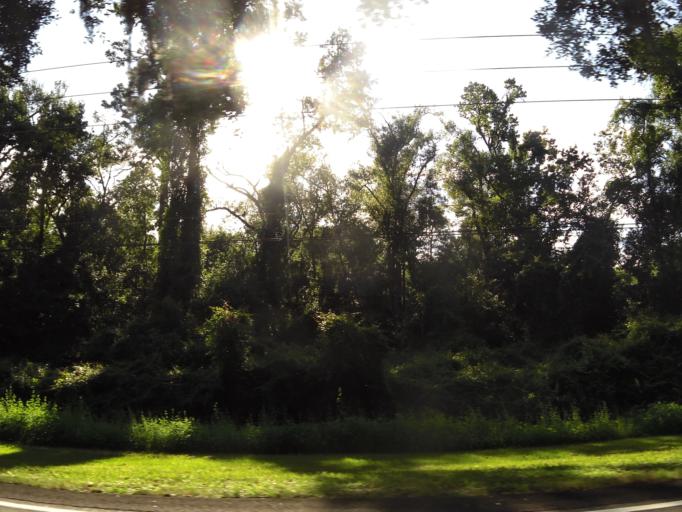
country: US
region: Georgia
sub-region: Glynn County
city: Saint Simon Mills
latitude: 31.1938
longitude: -81.3764
